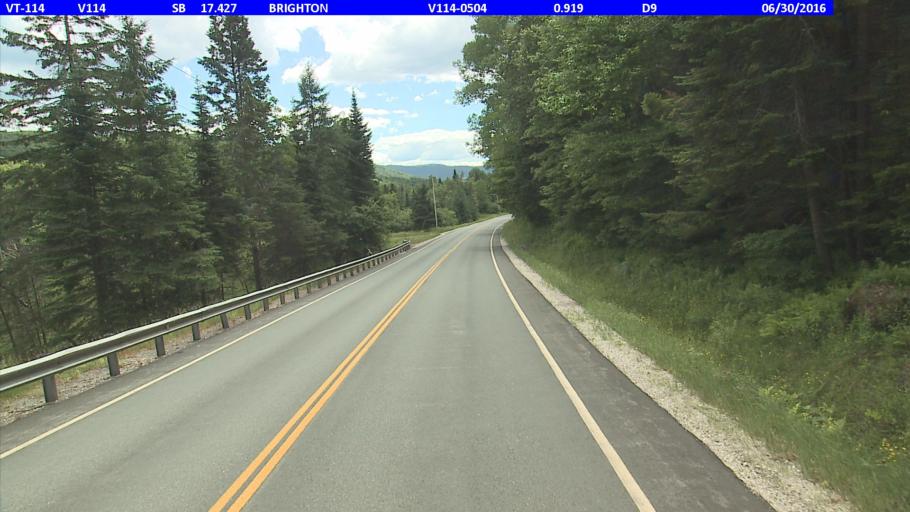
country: US
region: Vermont
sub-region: Caledonia County
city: Lyndonville
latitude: 44.7525
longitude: -71.8888
